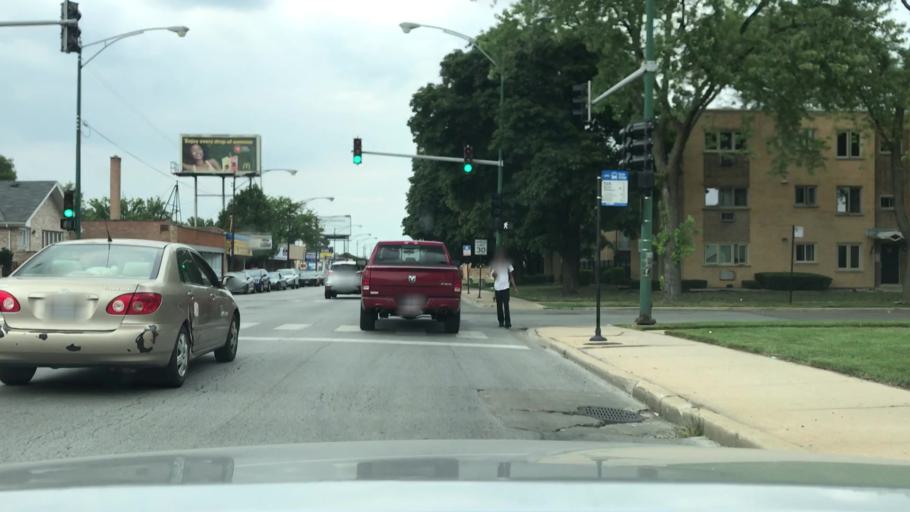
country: US
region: Illinois
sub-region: Cook County
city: Evergreen Park
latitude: 41.7387
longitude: -87.7020
